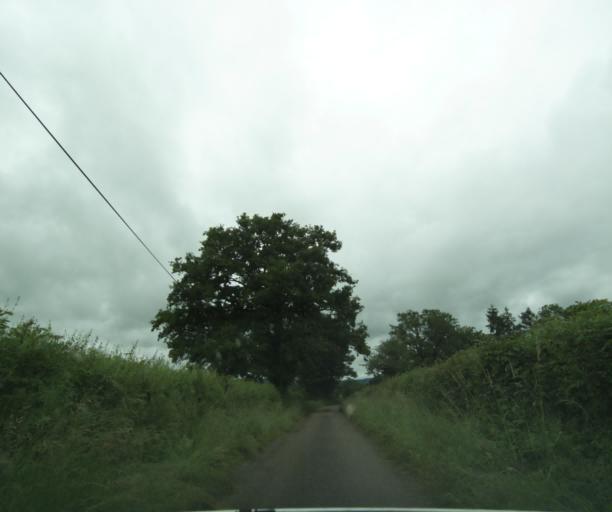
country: FR
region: Bourgogne
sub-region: Departement de Saone-et-Loire
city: Charolles
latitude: 46.4702
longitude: 4.3507
